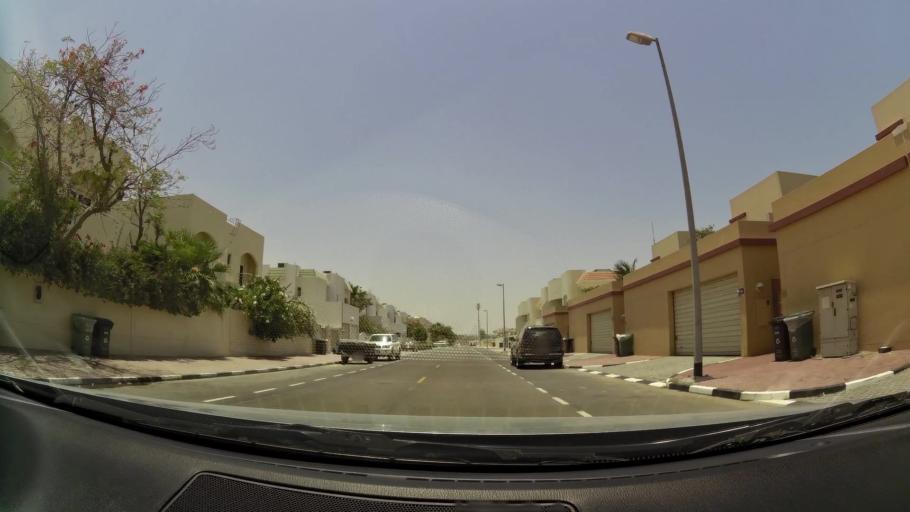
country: AE
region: Dubai
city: Dubai
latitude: 25.1759
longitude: 55.2301
